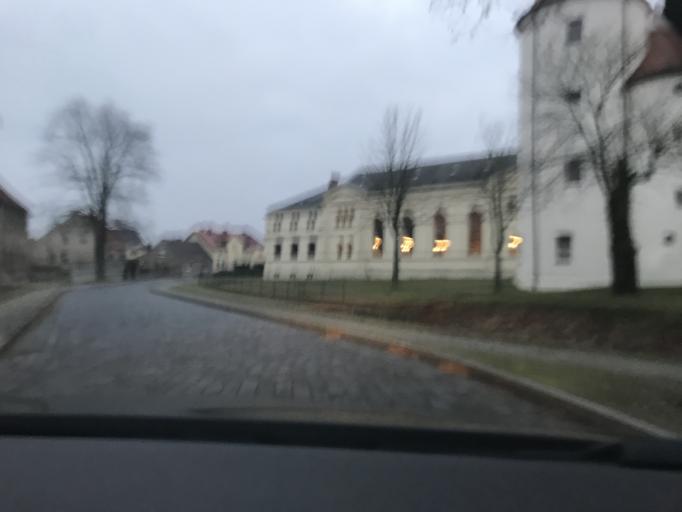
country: DE
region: Saxony-Anhalt
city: Annaburg
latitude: 51.7306
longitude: 13.0480
